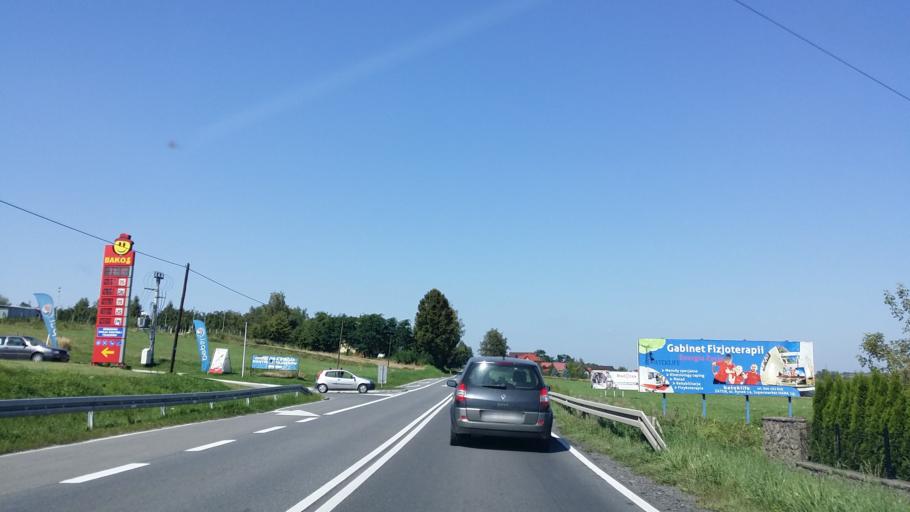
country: PL
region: Lesser Poland Voivodeship
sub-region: Powiat wadowicki
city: Radocza
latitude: 49.9182
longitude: 19.4816
